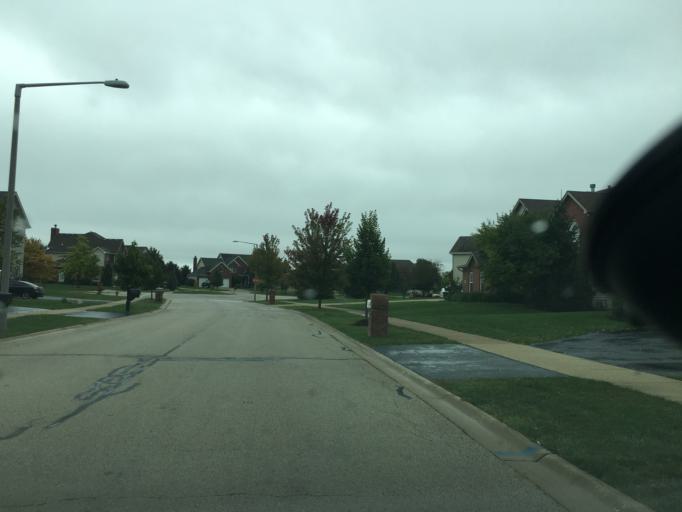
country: US
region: Illinois
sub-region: Will County
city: Plainfield
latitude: 41.6506
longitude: -88.2255
